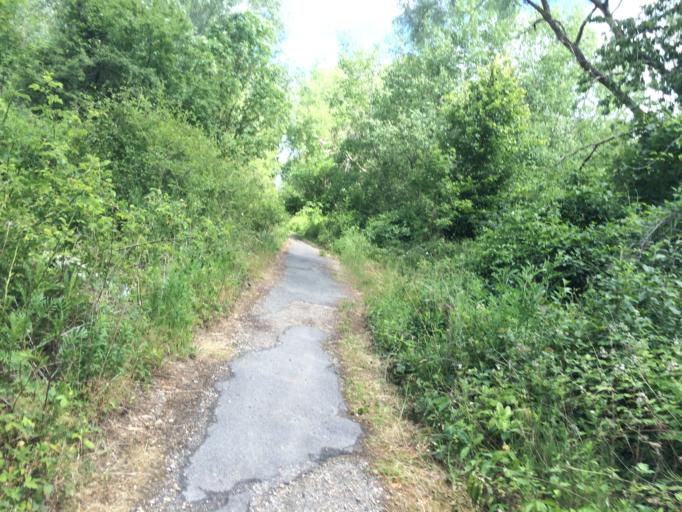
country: FR
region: Ile-de-France
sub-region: Departement de l'Essonne
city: Les Ulis
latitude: 48.6726
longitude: 2.1903
